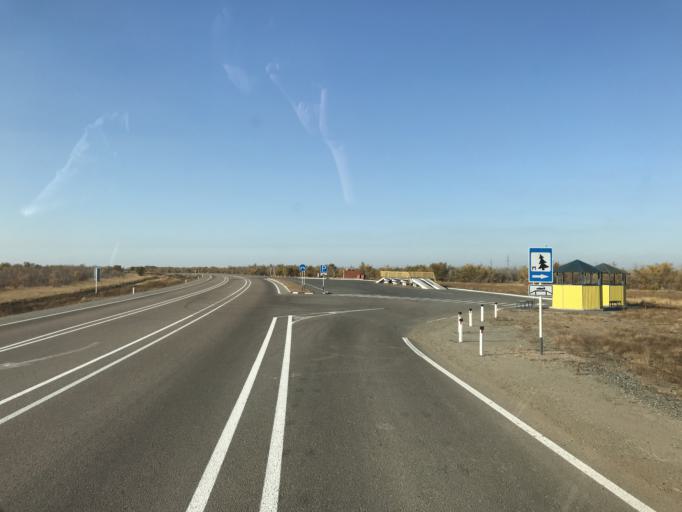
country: KZ
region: Pavlodar
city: Koktobe
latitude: 51.7272
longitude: 77.5601
